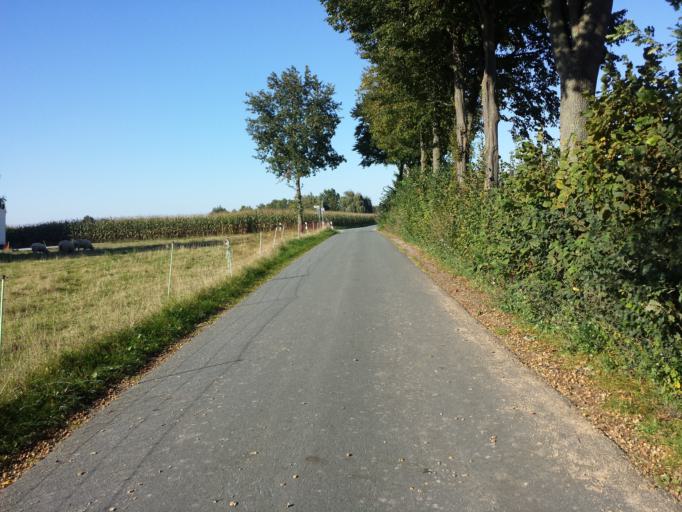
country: DE
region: North Rhine-Westphalia
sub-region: Regierungsbezirk Detmold
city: Langenberg
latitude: 51.7409
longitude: 8.3269
